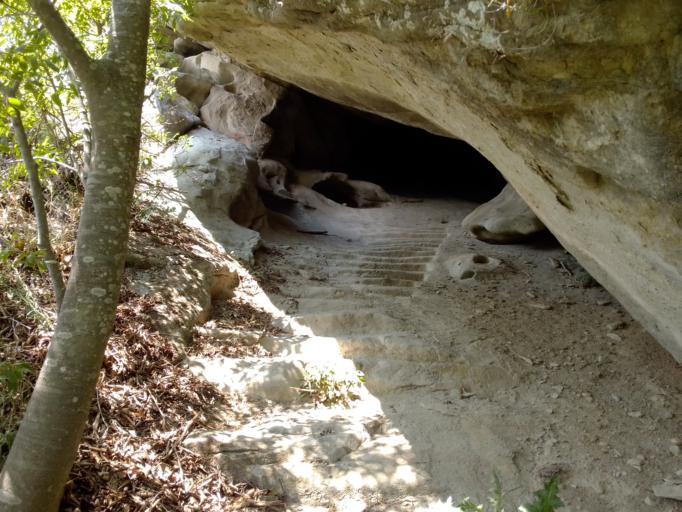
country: IT
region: Emilia-Romagna
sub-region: Provincia di Piacenza
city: Pianello Val Tidone
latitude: 44.9106
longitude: 9.3987
